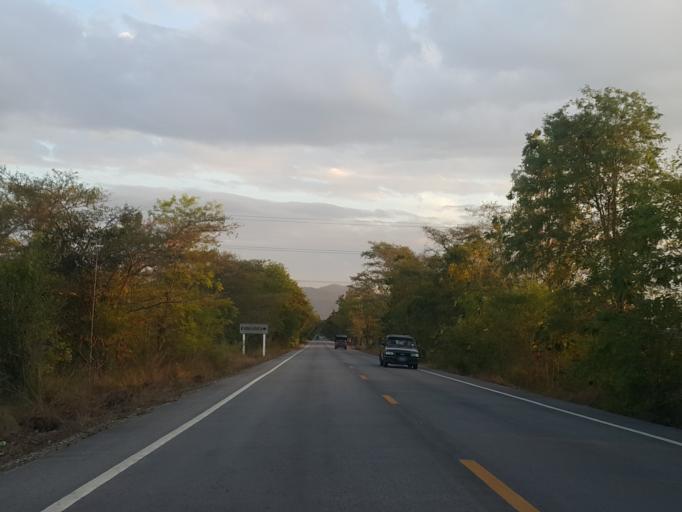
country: TH
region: Lampang
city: Mae Mo
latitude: 18.4366
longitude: 99.6404
